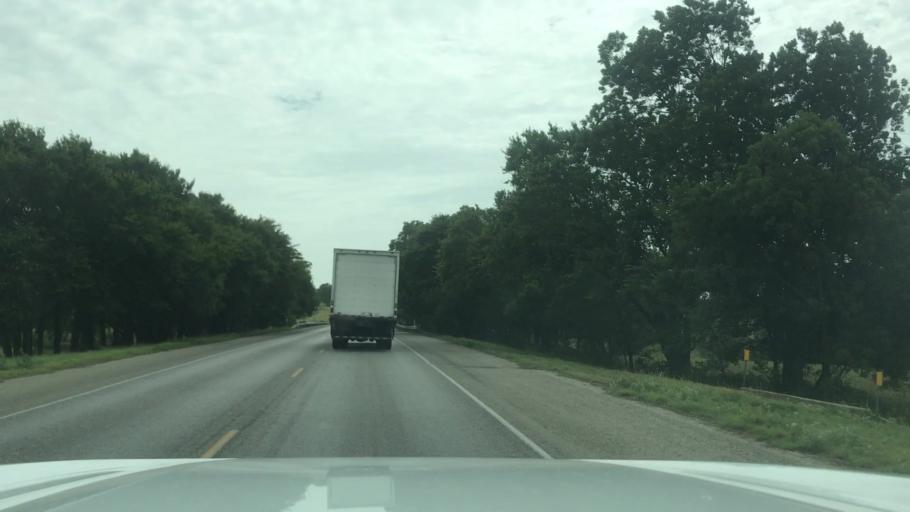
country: US
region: Texas
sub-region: Comanche County
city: De Leon
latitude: 32.0935
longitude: -98.4499
